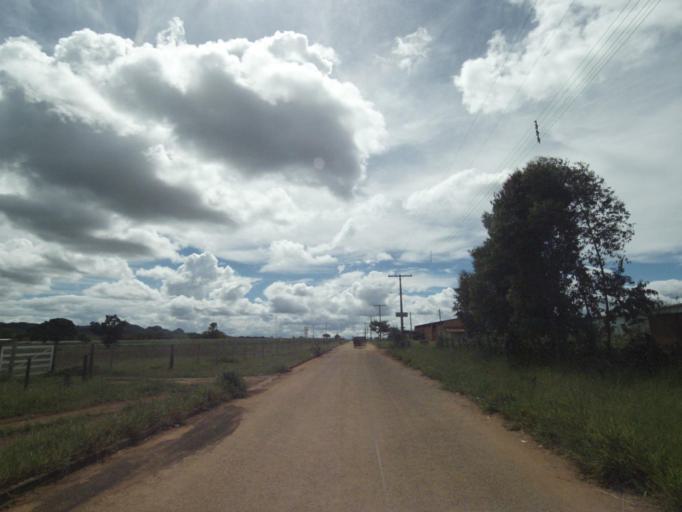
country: BR
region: Goias
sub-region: Pirenopolis
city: Pirenopolis
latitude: -15.7824
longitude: -48.7971
